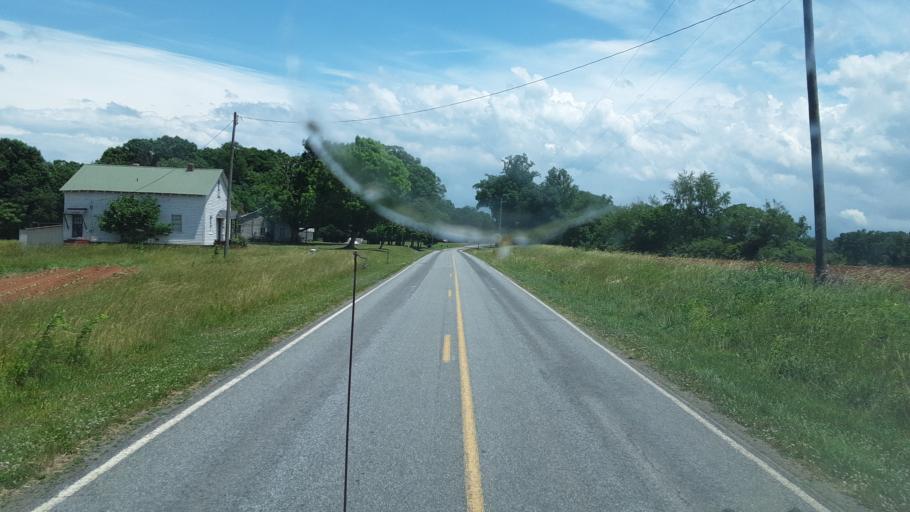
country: US
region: North Carolina
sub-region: Yadkin County
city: Jonesville
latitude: 36.0752
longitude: -80.8462
